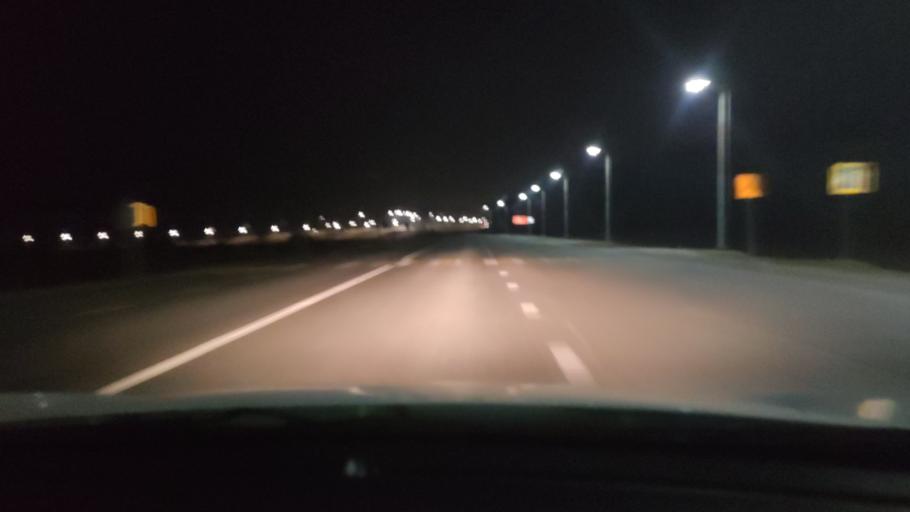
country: RU
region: Tatarstan
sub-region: Alekseyevskiy Rayon
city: Alekseyevskoye
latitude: 55.2974
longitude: 50.0454
